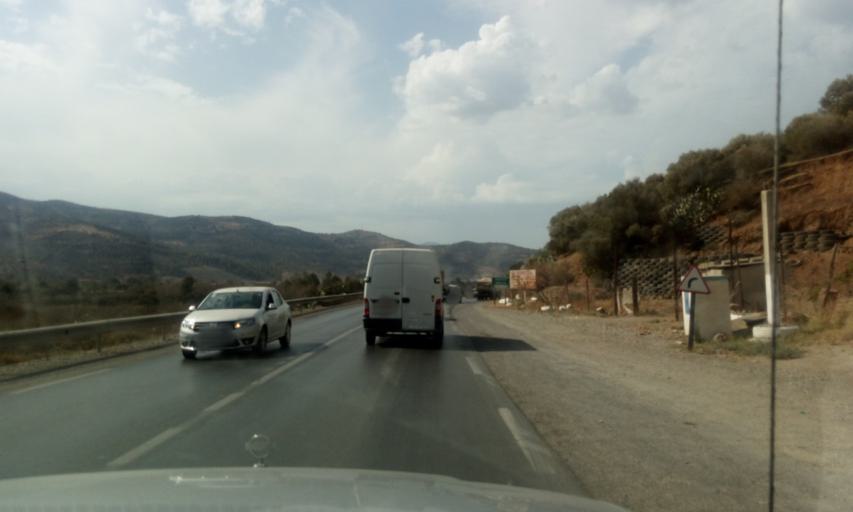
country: DZ
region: Bejaia
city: Seddouk
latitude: 36.5997
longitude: 4.6785
